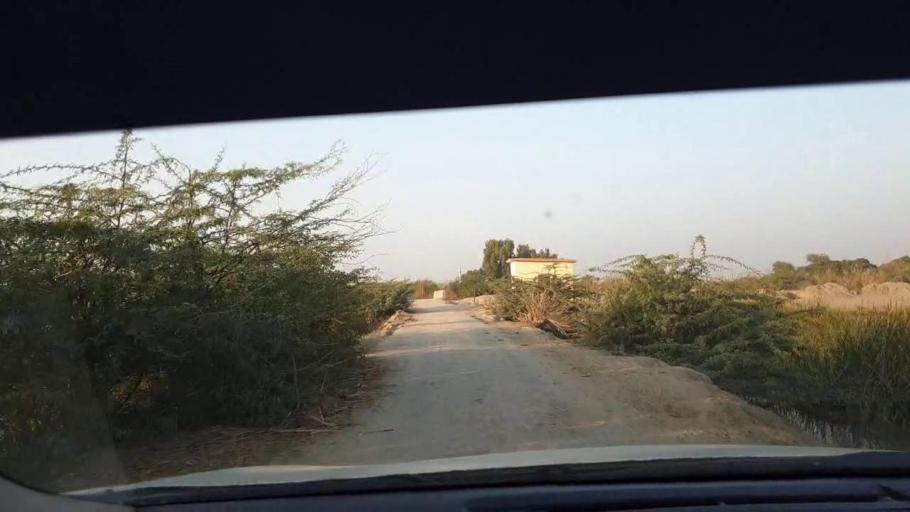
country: PK
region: Sindh
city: Berani
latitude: 25.8583
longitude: 68.8164
